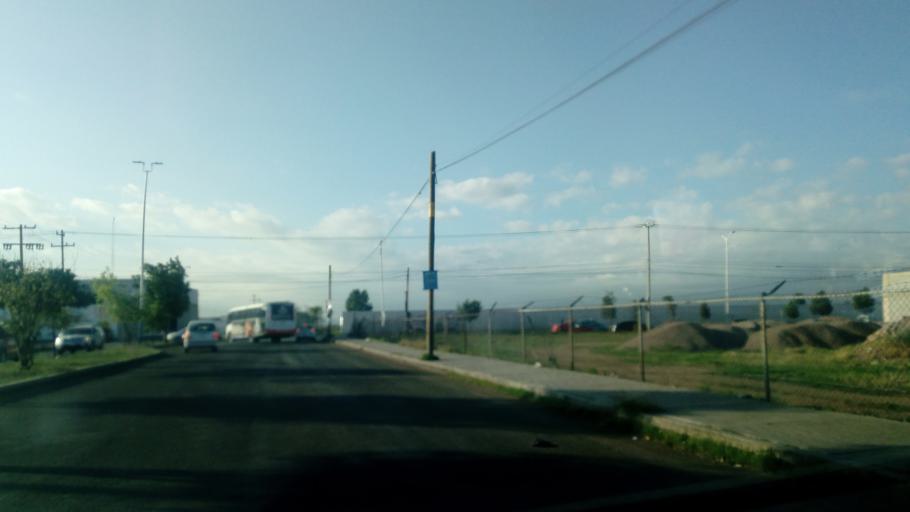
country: MX
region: Durango
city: Victoria de Durango
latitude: 24.0385
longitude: -104.6082
